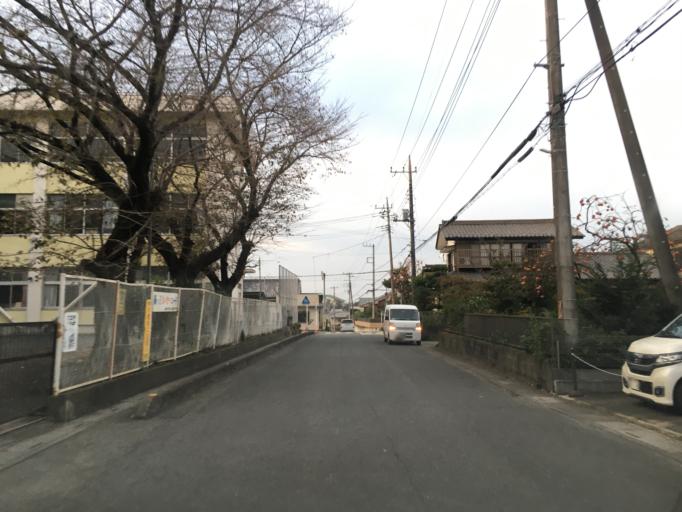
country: JP
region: Saitama
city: Sayama
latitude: 35.8984
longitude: 139.3745
